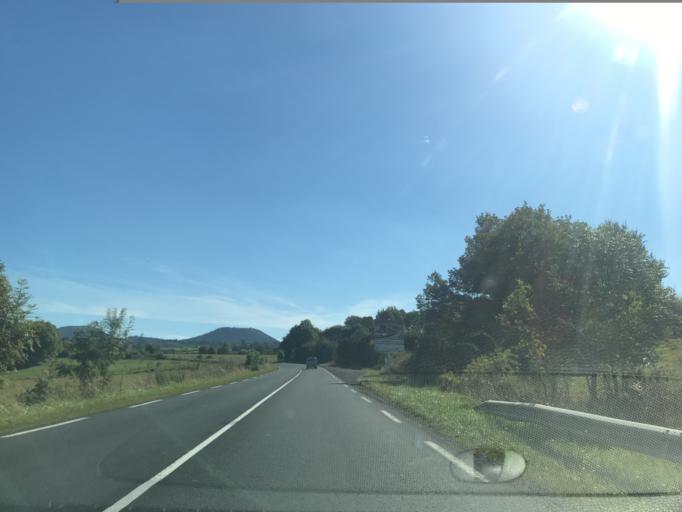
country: FR
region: Auvergne
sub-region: Departement du Puy-de-Dome
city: Aydat
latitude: 45.7304
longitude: 2.8778
